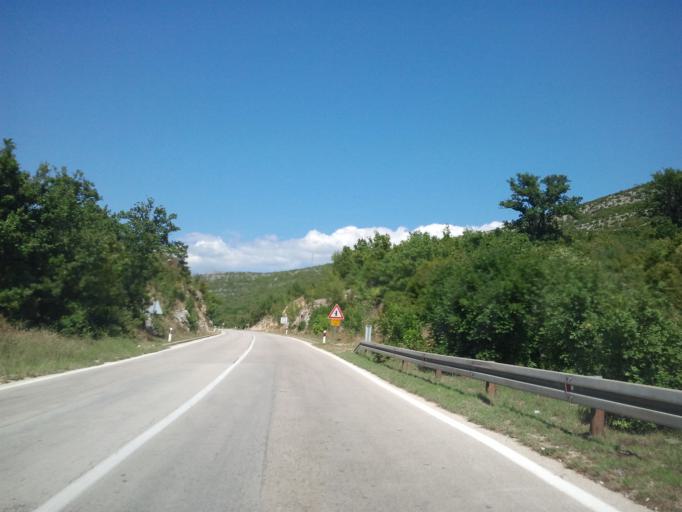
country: HR
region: Zadarska
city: Krusevo
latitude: 44.1626
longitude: 15.6267
